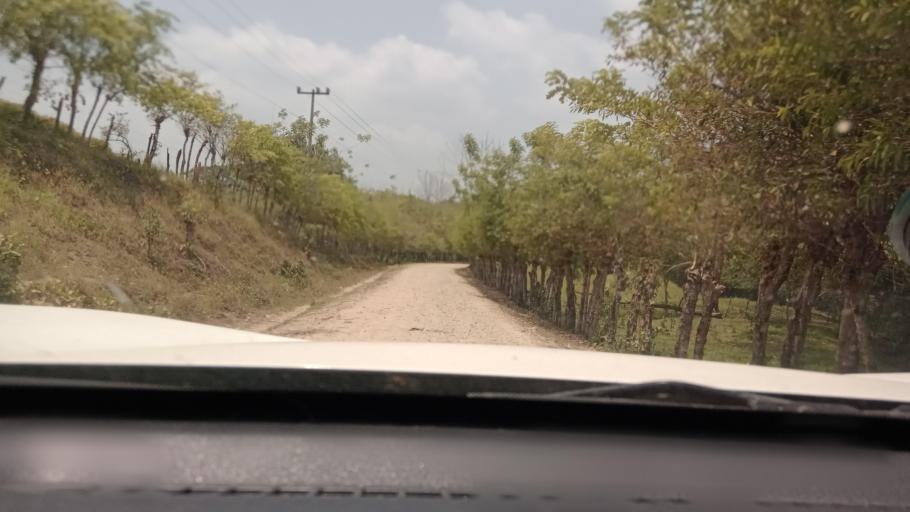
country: MX
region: Tabasco
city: Chontalpa
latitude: 17.5677
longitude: -93.7124
